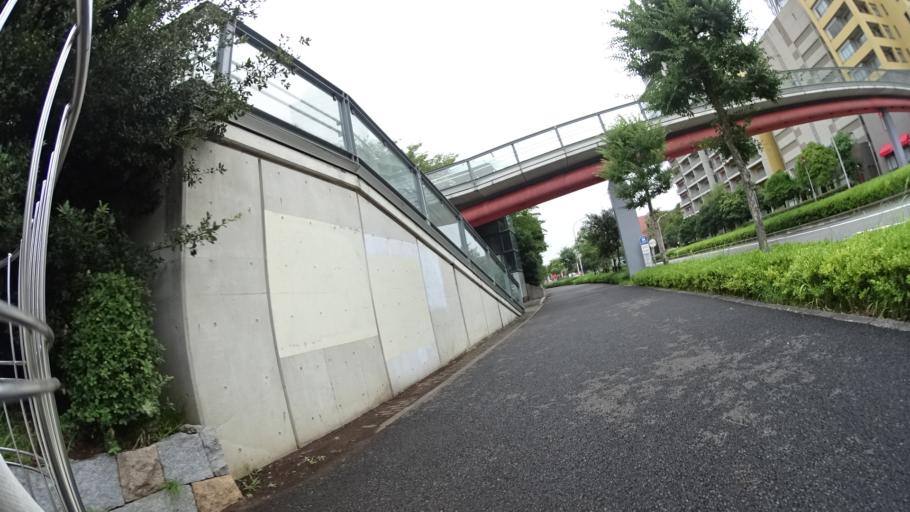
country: JP
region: Chiba
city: Funabashi
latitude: 35.6438
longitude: 140.0438
